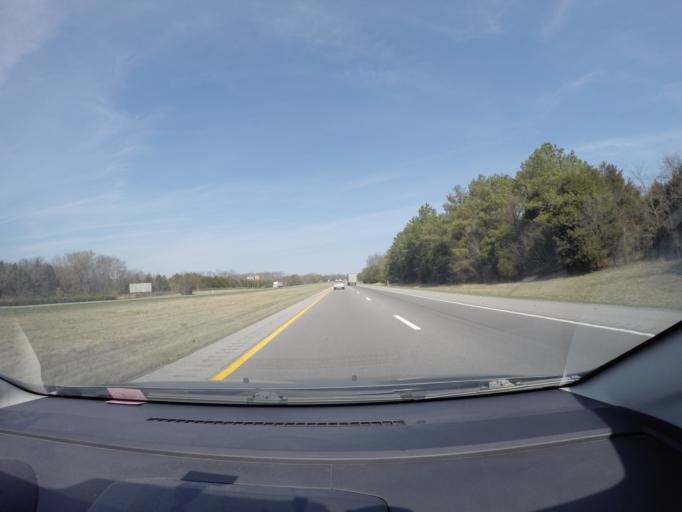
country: US
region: Tennessee
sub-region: Rutherford County
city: Plainview
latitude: 35.7706
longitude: -86.3616
